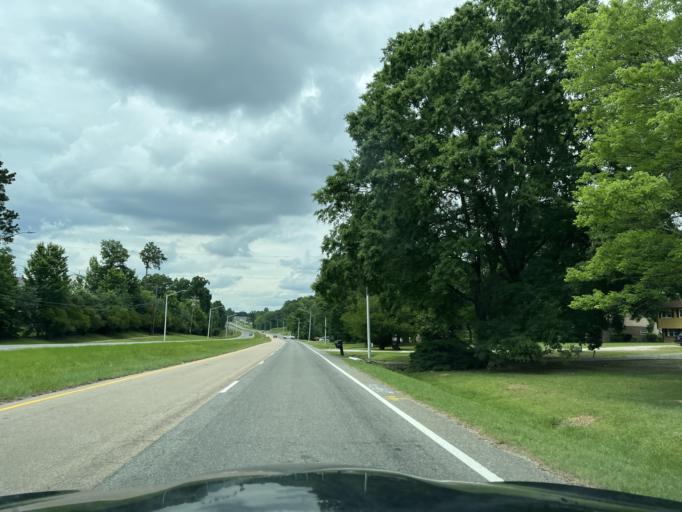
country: US
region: North Carolina
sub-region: Durham County
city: Durham
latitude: 35.9427
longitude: -78.8874
